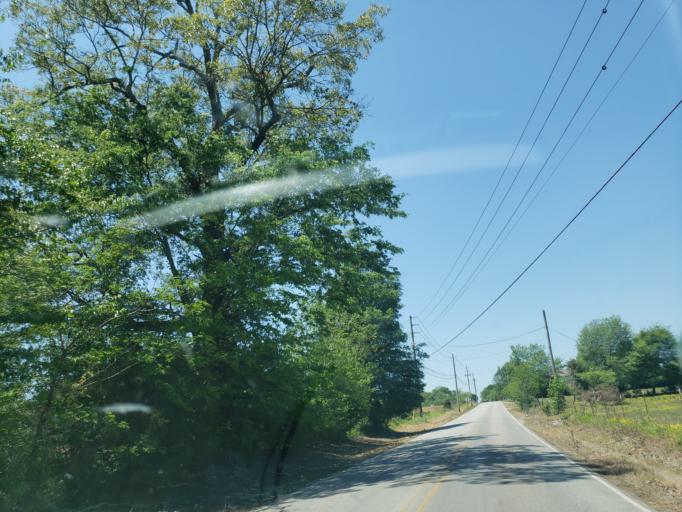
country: US
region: Alabama
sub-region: Madison County
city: Hazel Green
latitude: 34.9624
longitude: -86.6778
